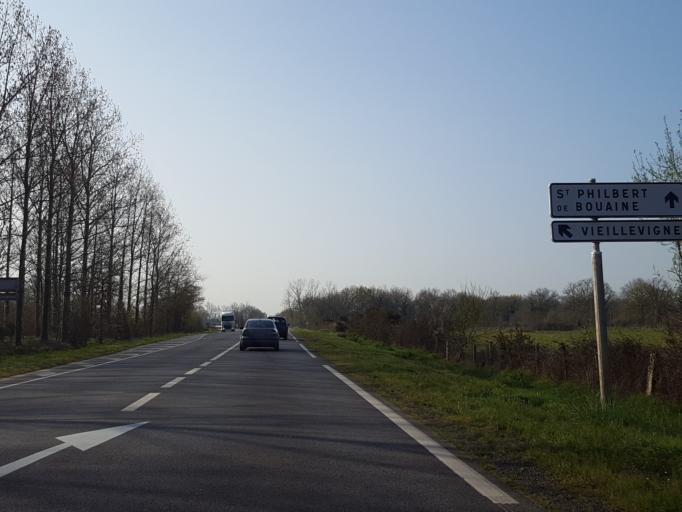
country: FR
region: Pays de la Loire
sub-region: Departement de la Loire-Atlantique
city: Geneston
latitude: 47.0399
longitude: -1.5074
